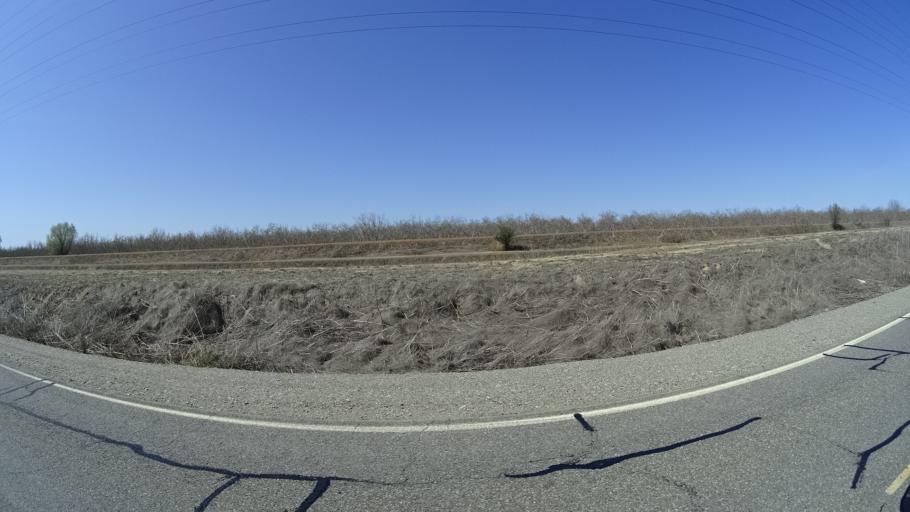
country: US
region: California
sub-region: Glenn County
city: Hamilton City
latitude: 39.7623
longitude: -122.0280
